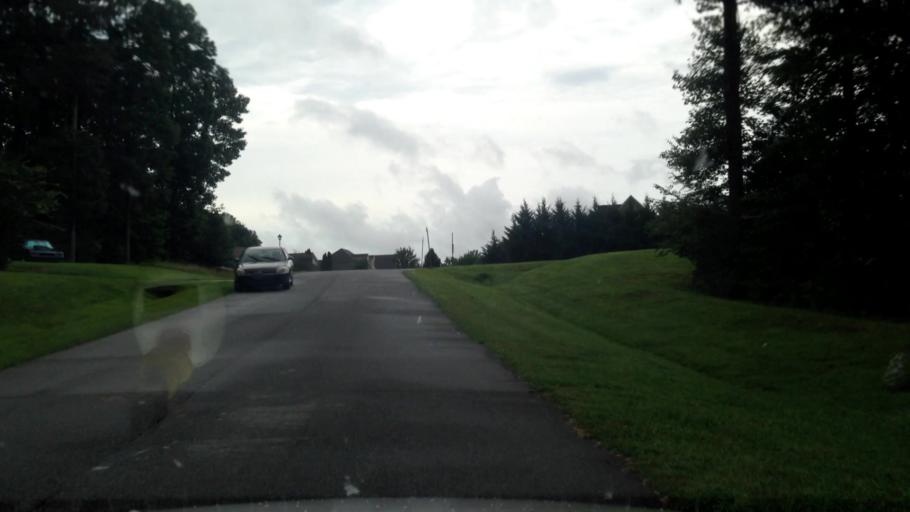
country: US
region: North Carolina
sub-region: Rockingham County
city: Reidsville
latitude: 36.2689
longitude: -79.7136
